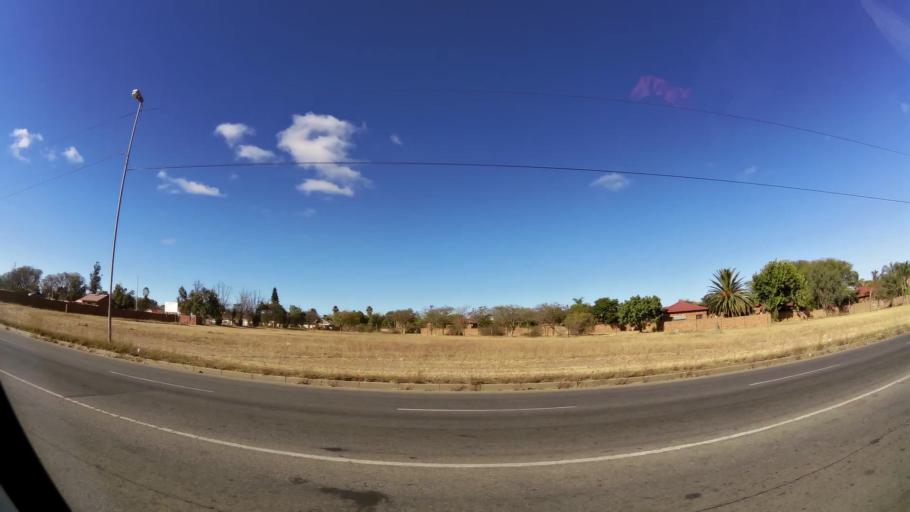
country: ZA
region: Limpopo
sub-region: Capricorn District Municipality
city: Polokwane
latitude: -23.8752
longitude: 29.4453
